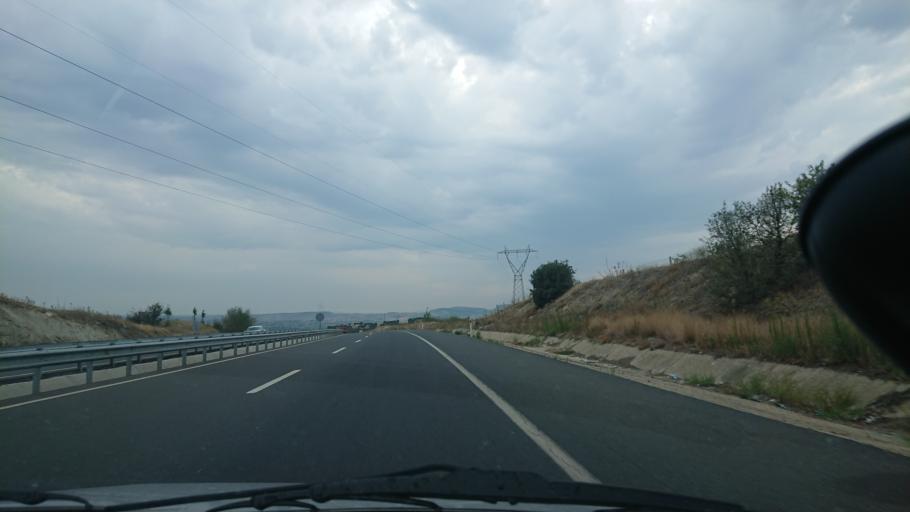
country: TR
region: Manisa
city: Selendi
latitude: 38.6279
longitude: 28.9339
